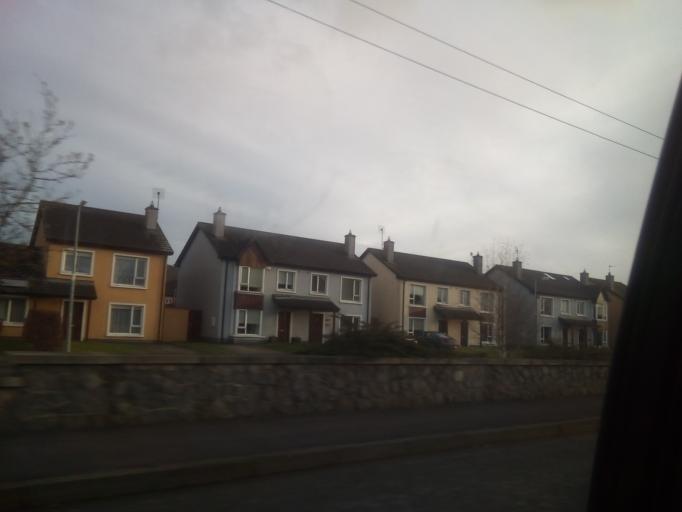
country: IE
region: Leinster
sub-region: Laois
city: Abbeyleix
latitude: 52.8415
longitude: -7.4039
